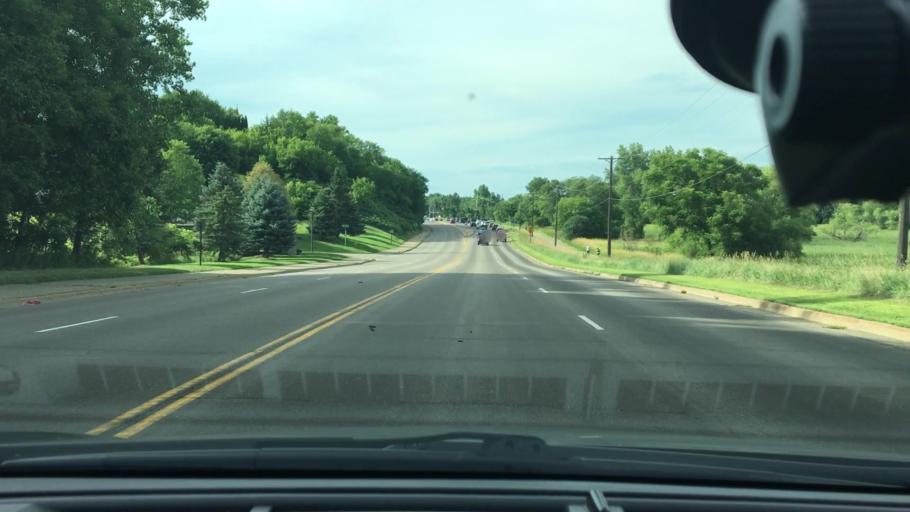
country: US
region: Minnesota
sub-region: Hennepin County
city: Plymouth
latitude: 45.0255
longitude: -93.4435
